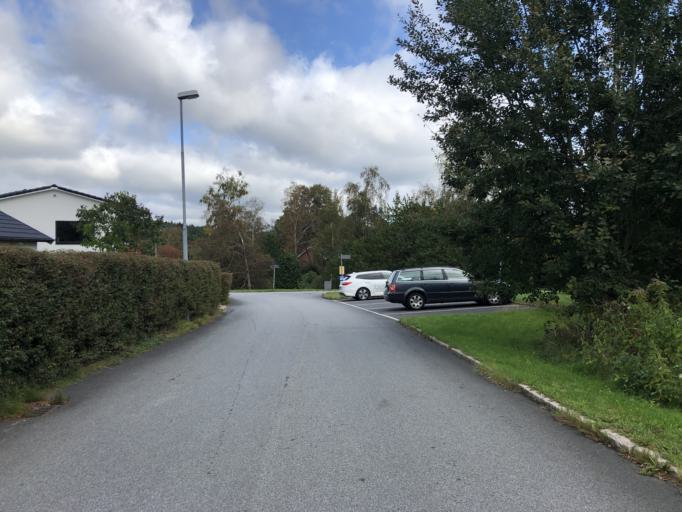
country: SE
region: Vaestra Goetaland
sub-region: Goteborg
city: Majorna
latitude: 57.7424
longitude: 11.8891
